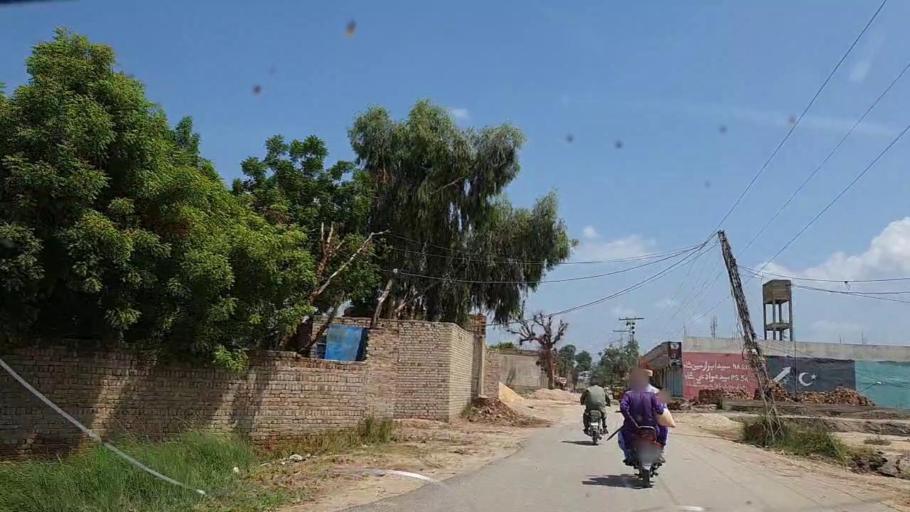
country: PK
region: Sindh
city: Tharu Shah
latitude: 26.9466
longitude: 68.1119
